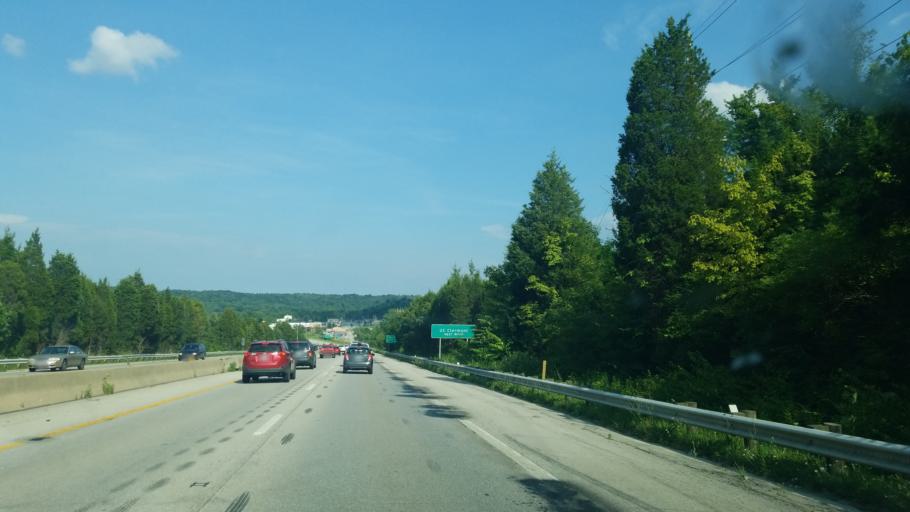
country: US
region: Ohio
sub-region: Clermont County
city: Batavia
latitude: 39.0856
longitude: -84.1987
